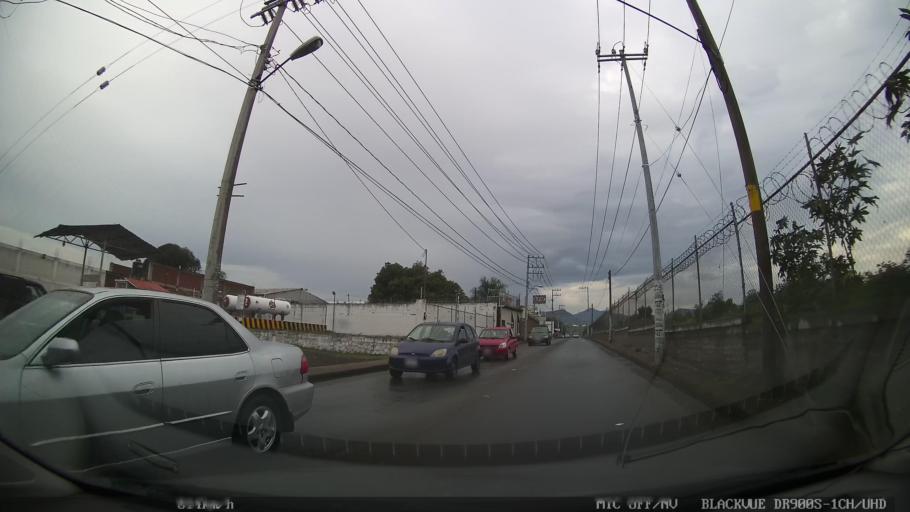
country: MX
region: Michoacan
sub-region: Uruapan
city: Santa Rosa (Santa Barbara)
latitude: 19.3823
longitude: -102.0453
